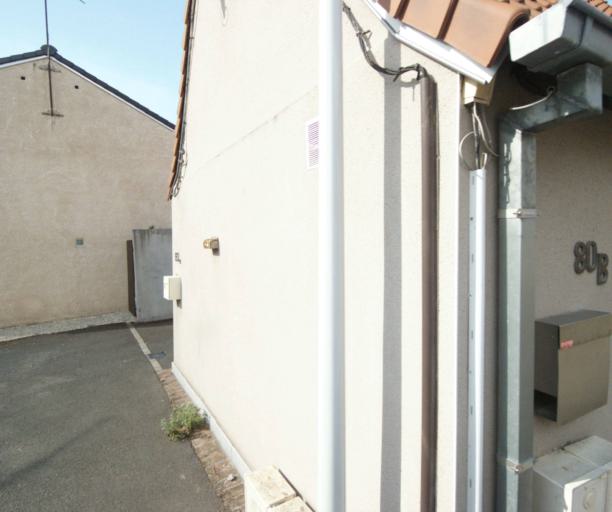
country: FR
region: Nord-Pas-de-Calais
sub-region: Departement du Nord
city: Sainghin-en-Melantois
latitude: 50.5898
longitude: 3.1662
